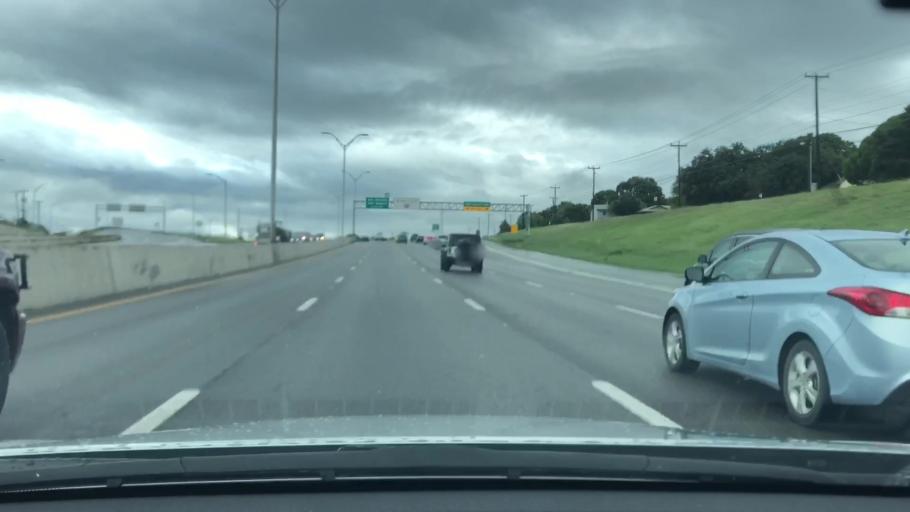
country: US
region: Texas
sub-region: Bexar County
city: Castle Hills
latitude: 29.5415
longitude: -98.4920
